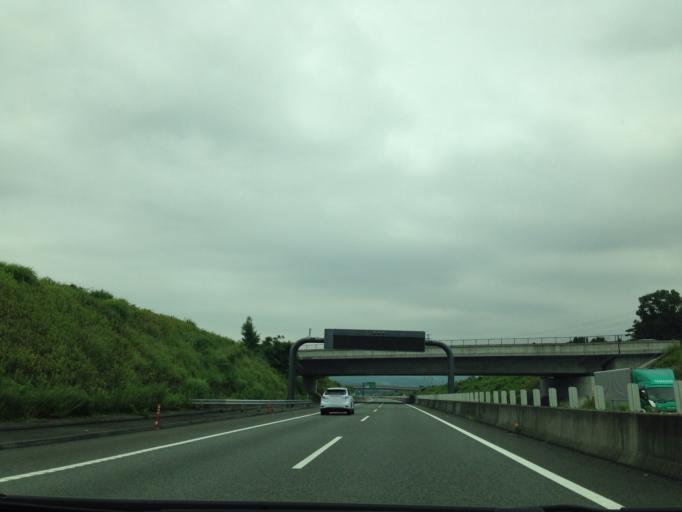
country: JP
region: Shizuoka
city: Fuji
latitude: 35.2015
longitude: 138.6805
